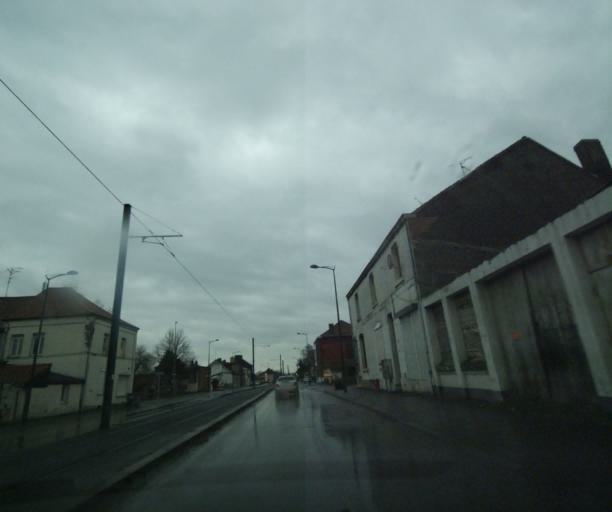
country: FR
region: Nord-Pas-de-Calais
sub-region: Departement du Nord
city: Fresnes-sur-Escaut
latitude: 50.4263
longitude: 3.5665
